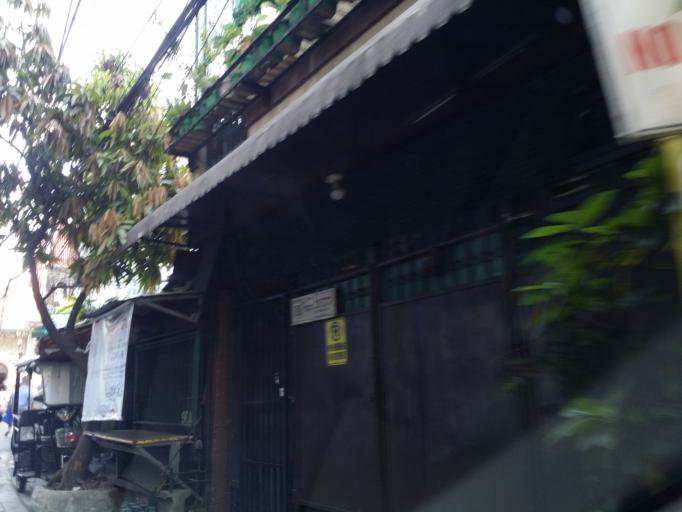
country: PH
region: Metro Manila
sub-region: Mandaluyong
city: Mandaluyong City
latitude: 14.5867
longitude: 121.0266
